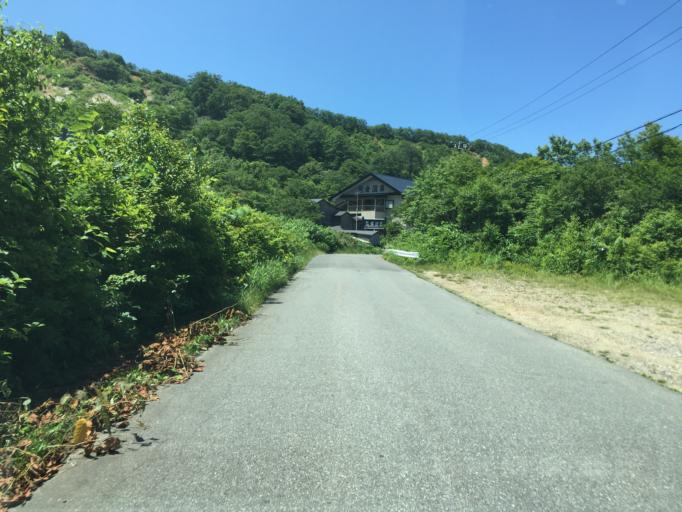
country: JP
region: Fukushima
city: Inawashiro
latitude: 37.6693
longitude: 140.2621
